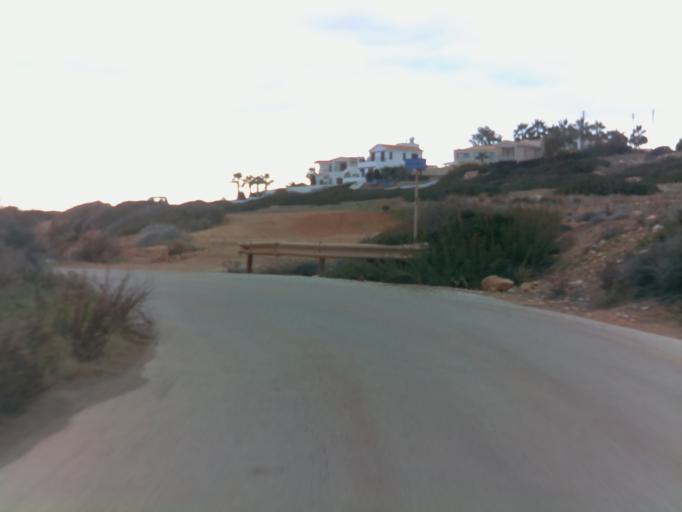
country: CY
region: Pafos
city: Pegeia
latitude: 34.8840
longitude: 32.3339
